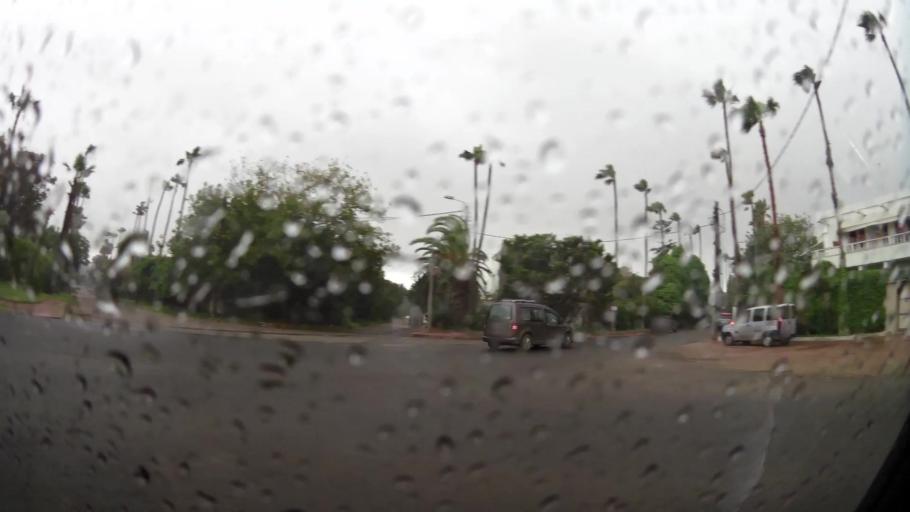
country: MA
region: Grand Casablanca
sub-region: Casablanca
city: Casablanca
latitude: 33.5885
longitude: -7.6787
